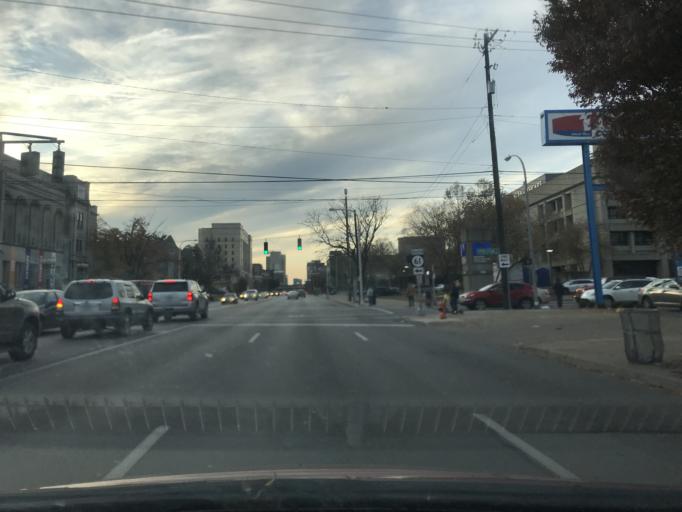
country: US
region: Kentucky
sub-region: Jefferson County
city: Louisville
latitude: 38.2453
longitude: -85.7472
